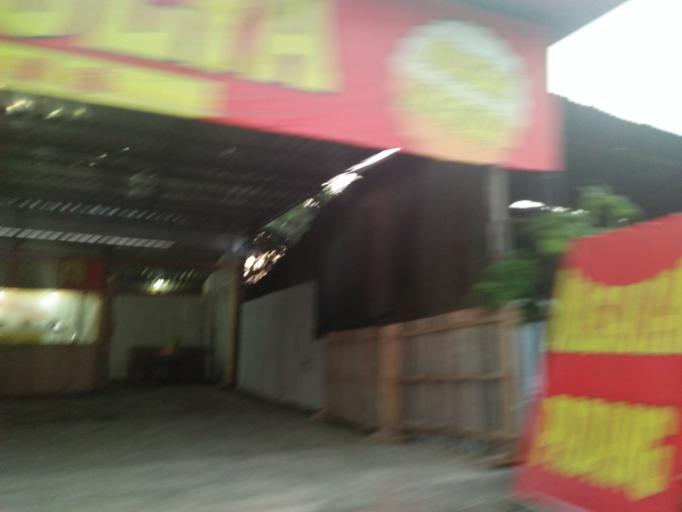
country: ID
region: Daerah Istimewa Yogyakarta
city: Sewon
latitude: -7.8423
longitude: 110.3913
